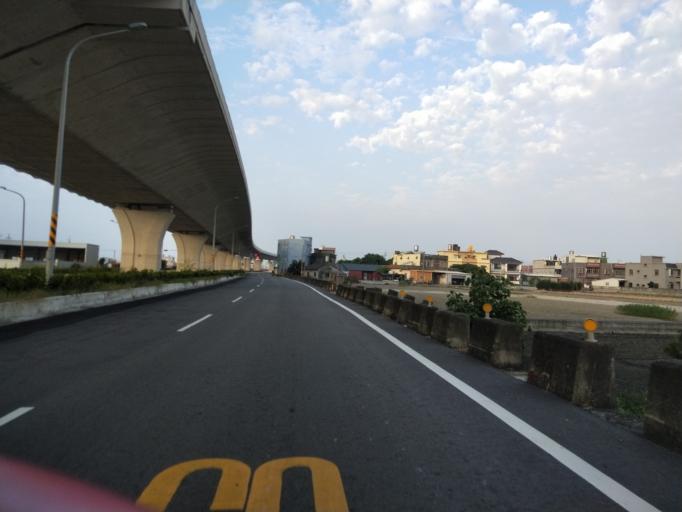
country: TW
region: Taiwan
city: Fengyuan
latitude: 24.4277
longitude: 120.6264
